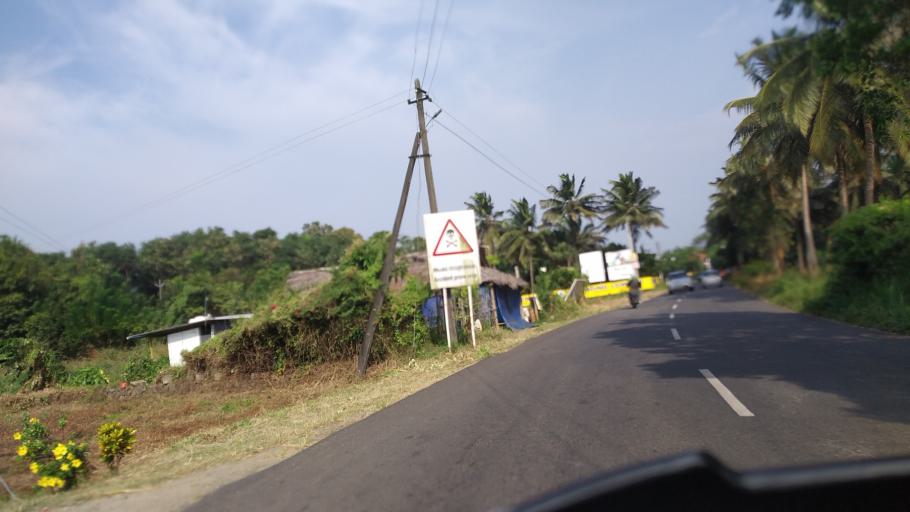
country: IN
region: Kerala
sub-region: Thrissur District
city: Chelakara
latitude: 10.5995
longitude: 76.5337
